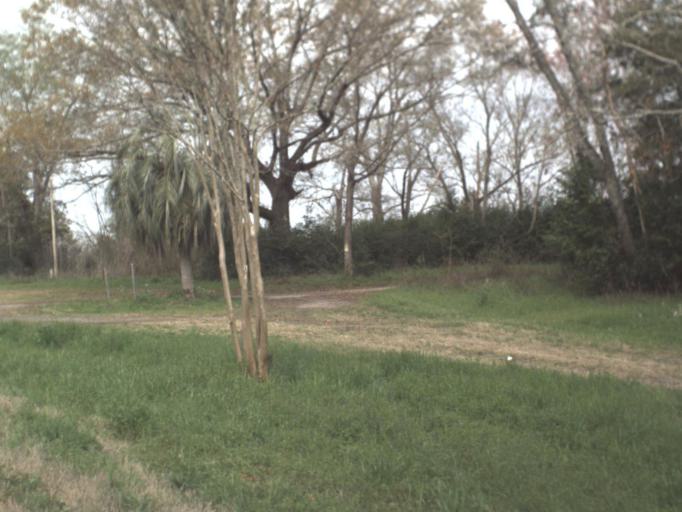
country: US
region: Florida
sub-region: Jefferson County
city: Monticello
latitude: 30.5233
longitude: -84.0263
